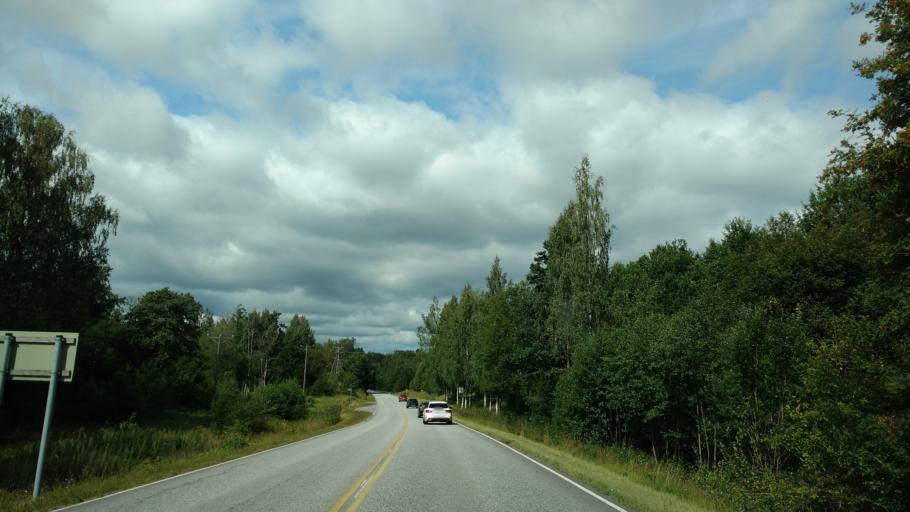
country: FI
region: Varsinais-Suomi
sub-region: Salo
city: Saerkisalo
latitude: 60.1882
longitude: 22.8843
